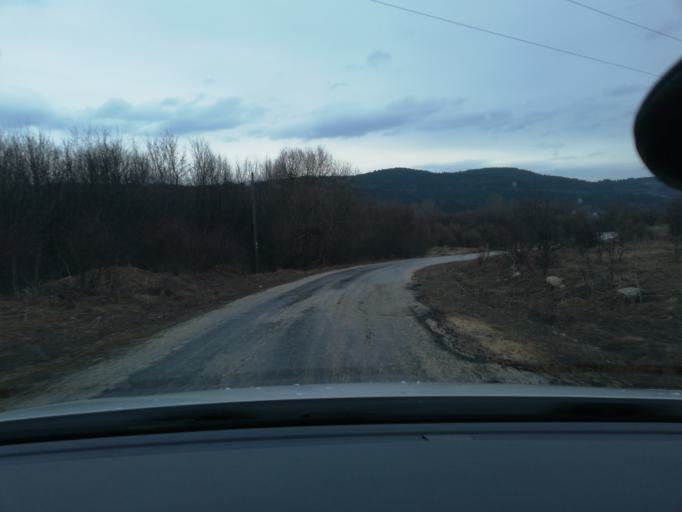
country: TR
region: Bolu
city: Yenicaga
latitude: 40.7532
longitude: 31.9299
